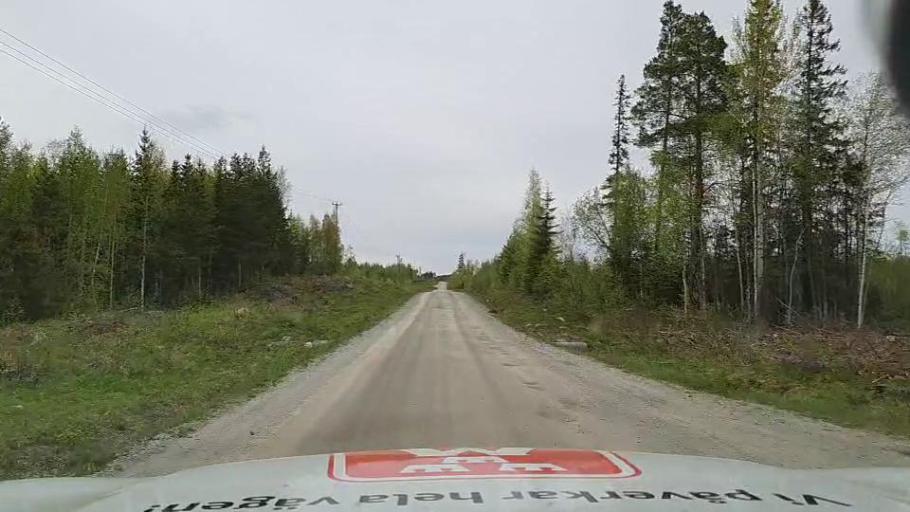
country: SE
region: Jaemtland
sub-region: Bergs Kommun
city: Hoverberg
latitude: 62.8355
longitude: 14.6659
